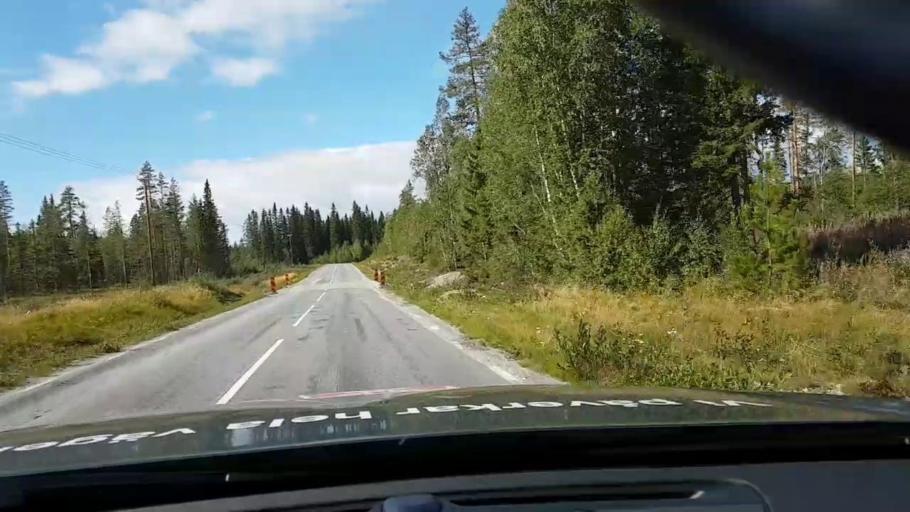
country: SE
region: Vaesterbotten
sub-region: Asele Kommun
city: Asele
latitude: 63.8233
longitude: 17.4806
